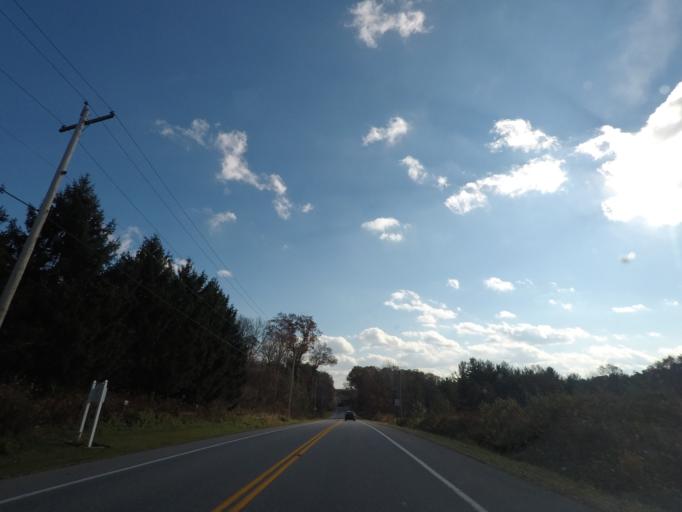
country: US
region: New York
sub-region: Schenectady County
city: East Glenville
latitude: 42.9007
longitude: -73.8952
